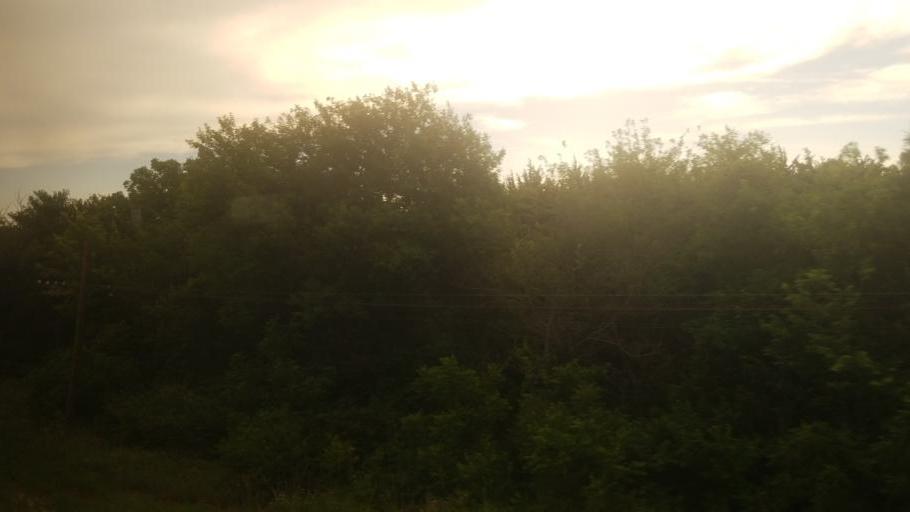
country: US
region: Kansas
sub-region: Osage County
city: Carbondale
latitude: 38.9294
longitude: -95.6905
